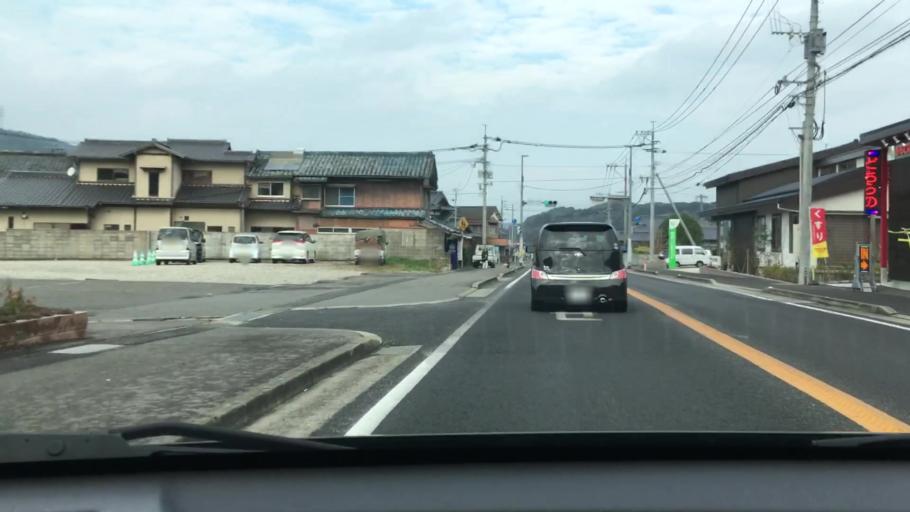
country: JP
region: Saga Prefecture
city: Imaricho-ko
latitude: 33.3103
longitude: 129.9280
